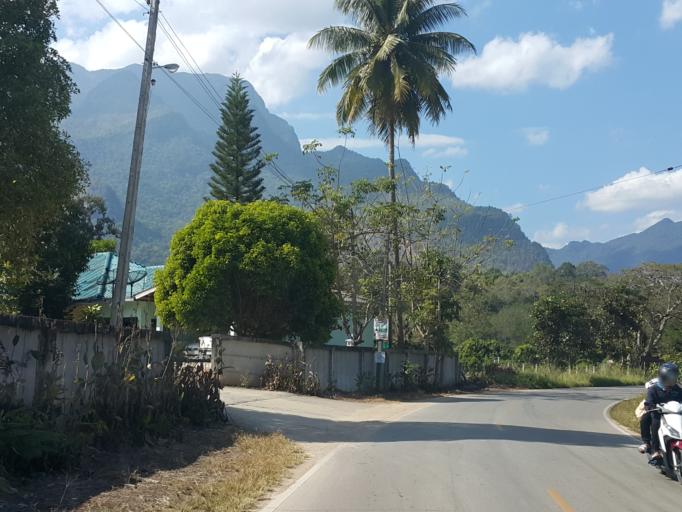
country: TH
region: Chiang Mai
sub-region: Amphoe Chiang Dao
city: Chiang Dao
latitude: 19.3781
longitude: 98.9447
